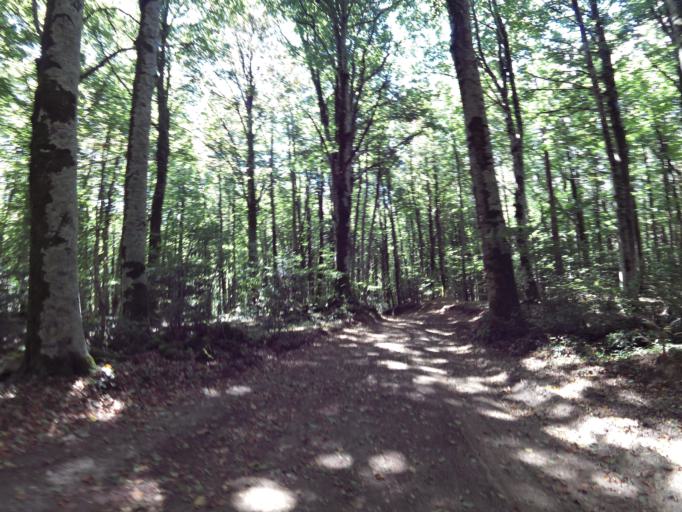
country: IT
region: Calabria
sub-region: Provincia di Vibo-Valentia
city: Mongiana
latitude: 38.5209
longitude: 16.3447
